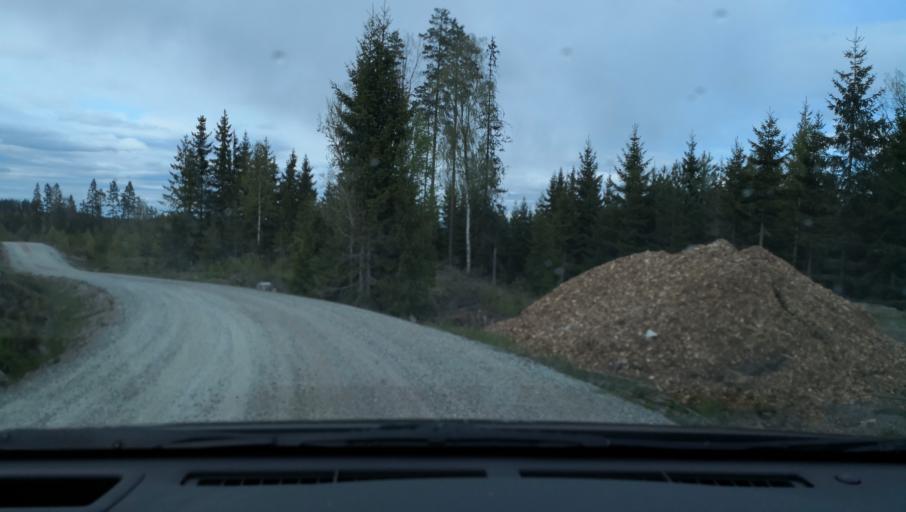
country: SE
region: Dalarna
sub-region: Saters Kommun
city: Saeter
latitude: 60.1917
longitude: 15.7405
